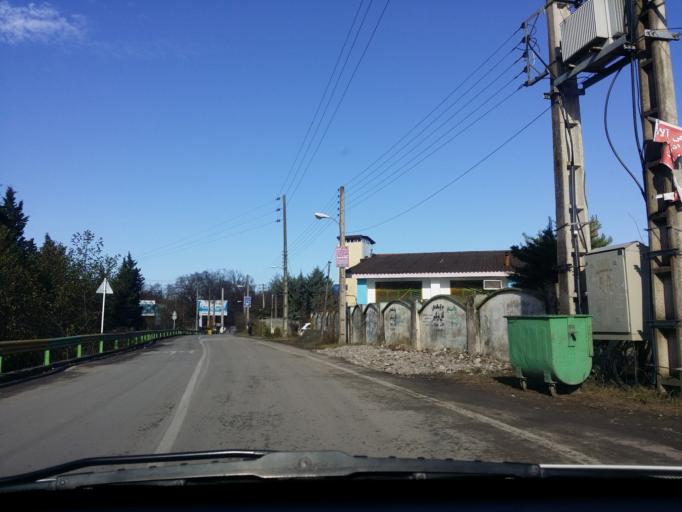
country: IR
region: Mazandaran
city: Chalus
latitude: 36.6863
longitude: 51.3134
